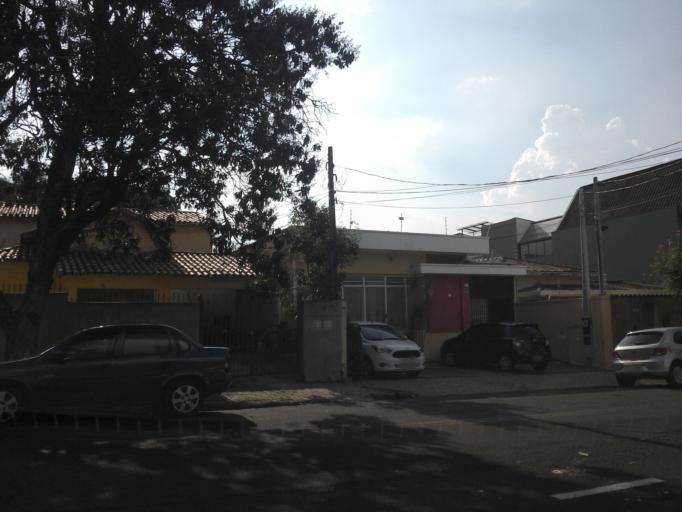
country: BR
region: Sao Paulo
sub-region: Campinas
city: Campinas
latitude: -22.8890
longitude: -47.0667
